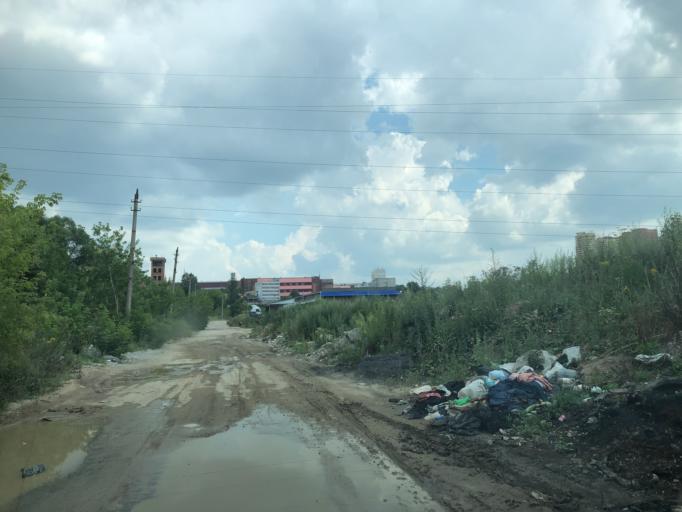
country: RU
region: Tula
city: Mendeleyevskiy
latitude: 54.1604
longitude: 37.5735
